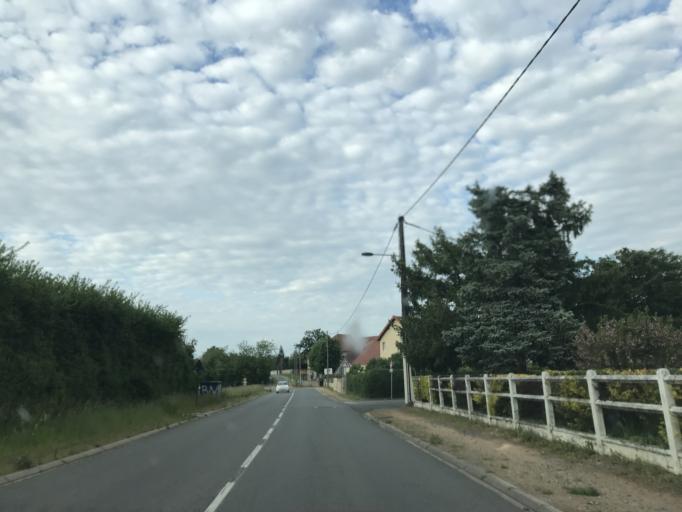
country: FR
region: Auvergne
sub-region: Departement de l'Allier
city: Bellerive-sur-Allier
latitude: 46.0975
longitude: 3.4012
